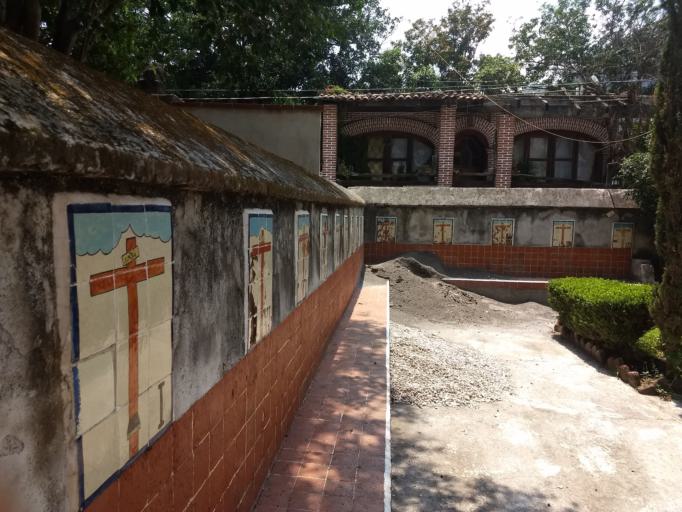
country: MX
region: Morelos
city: Tepoztlan
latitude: 18.9892
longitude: -99.0949
